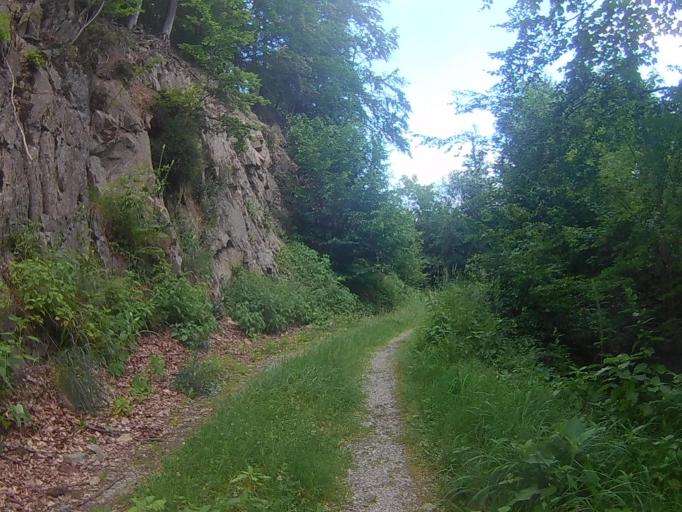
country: SI
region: Selnica ob Dravi
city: Selnica ob Dravi
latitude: 46.5195
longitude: 15.4858
